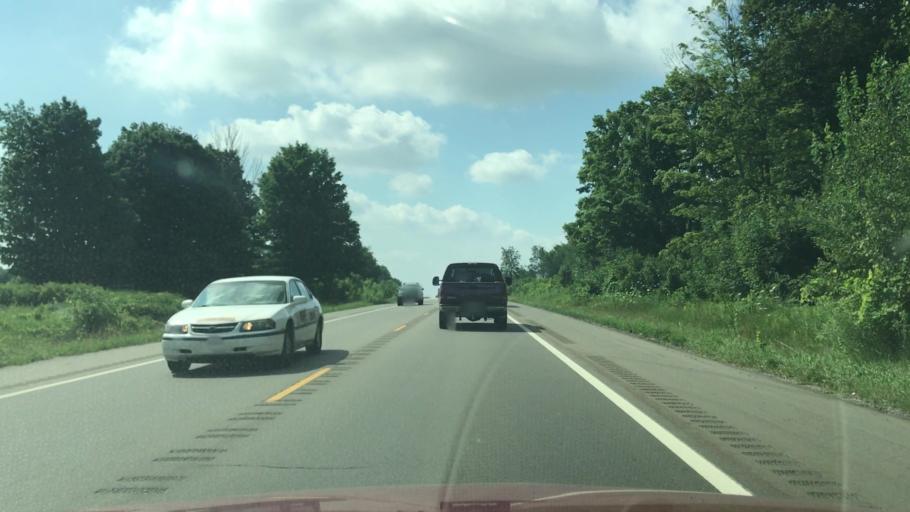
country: US
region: Michigan
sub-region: Kent County
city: Sparta
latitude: 43.1353
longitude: -85.7164
